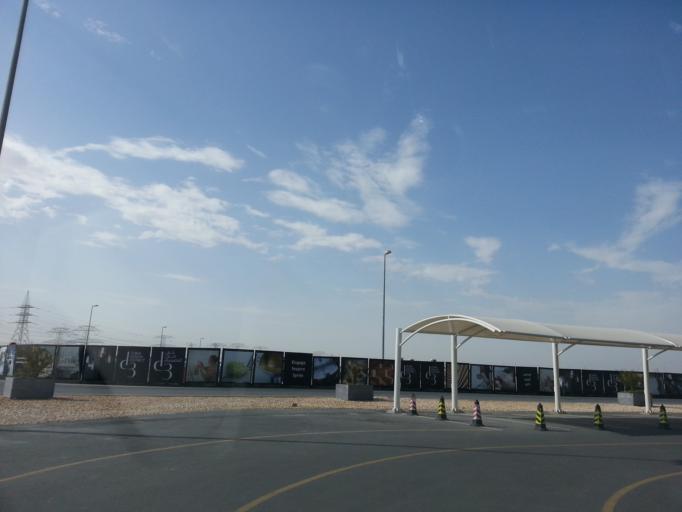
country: AE
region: Dubai
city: Dubai
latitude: 25.1875
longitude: 55.2996
